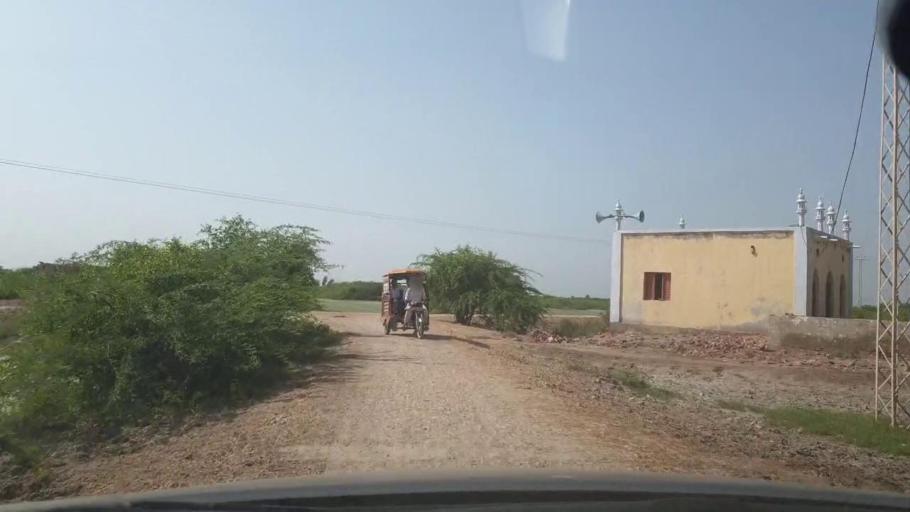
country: PK
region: Sindh
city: Naukot
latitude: 24.8015
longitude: 69.2403
